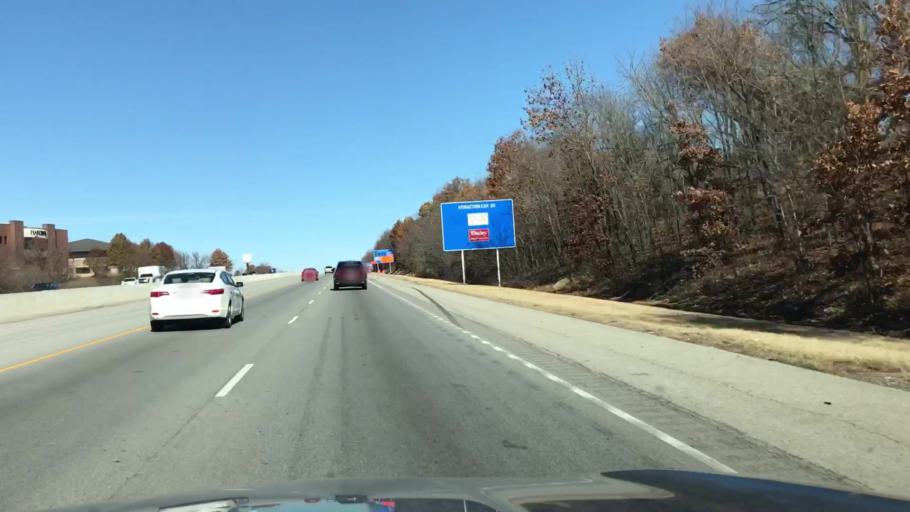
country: US
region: Arkansas
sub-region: Benton County
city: Bentonville
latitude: 36.3221
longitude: -94.1848
